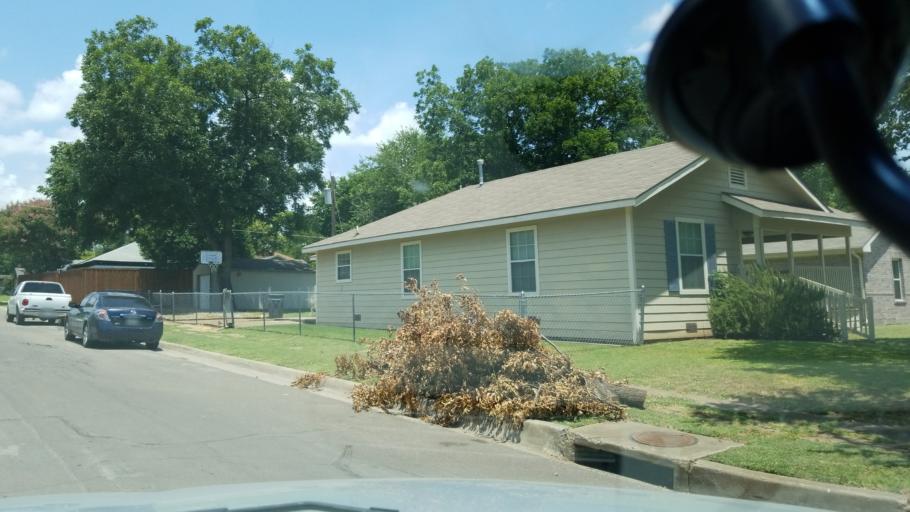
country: US
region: Texas
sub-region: Dallas County
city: Cockrell Hill
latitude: 32.7321
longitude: -96.8592
